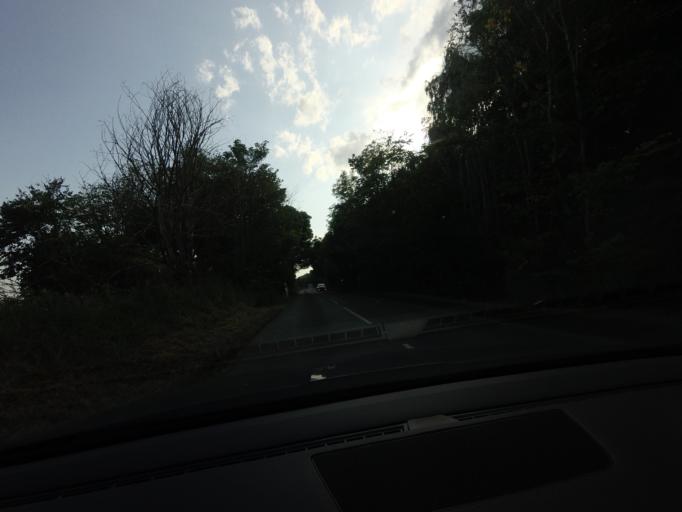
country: GB
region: Scotland
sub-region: Highland
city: Dingwall
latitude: 57.6213
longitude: -4.3851
